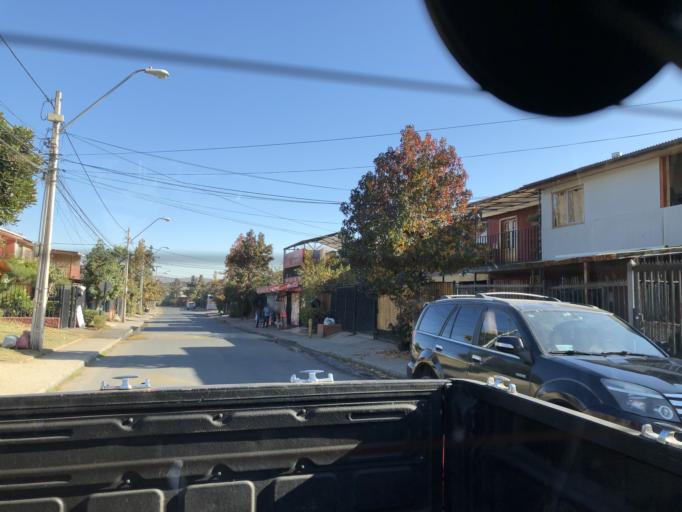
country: CL
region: Santiago Metropolitan
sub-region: Provincia de Cordillera
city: Puente Alto
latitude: -33.5940
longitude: -70.5558
